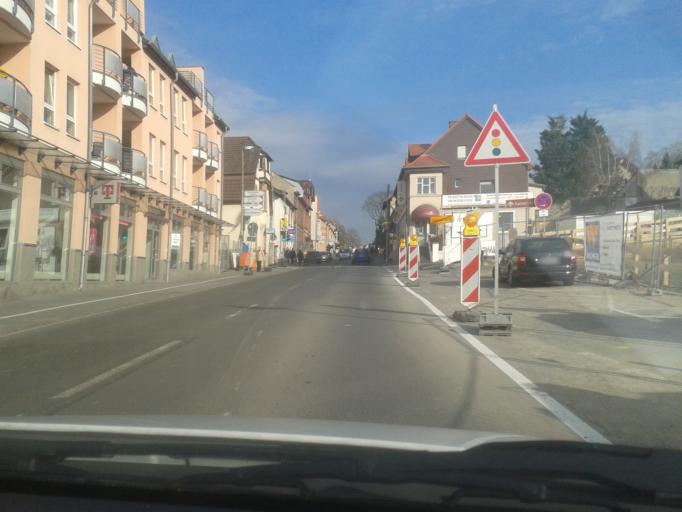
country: DE
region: Rheinland-Pfalz
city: Ingelheim am Rhein
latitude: 49.9750
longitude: 8.0577
